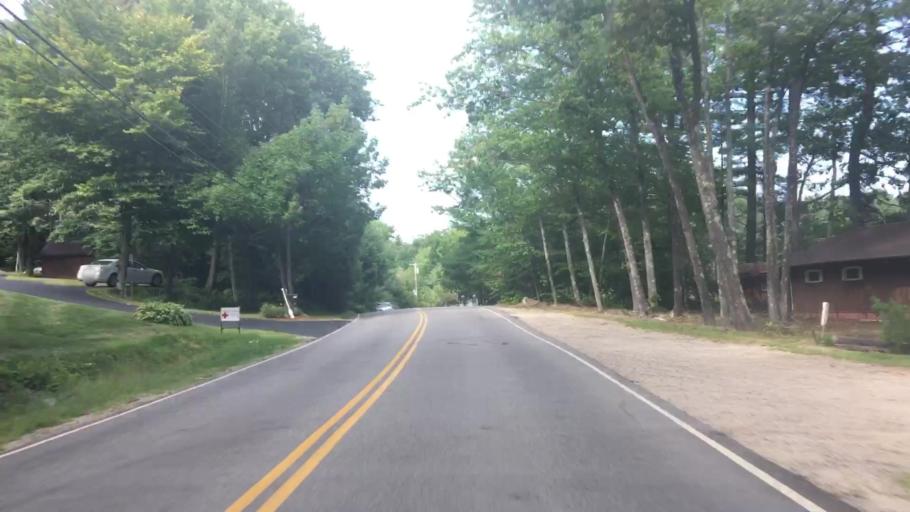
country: US
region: Maine
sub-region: Oxford County
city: Oxford
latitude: 44.1088
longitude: -70.5077
